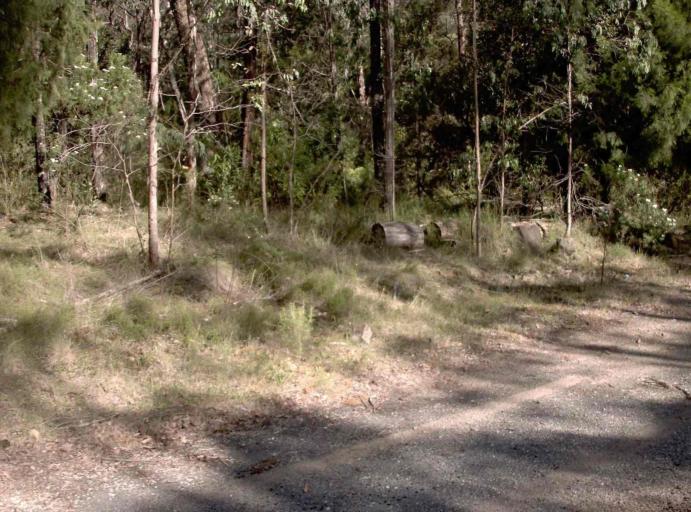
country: AU
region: Victoria
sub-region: East Gippsland
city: Lakes Entrance
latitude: -37.4772
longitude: 148.5562
